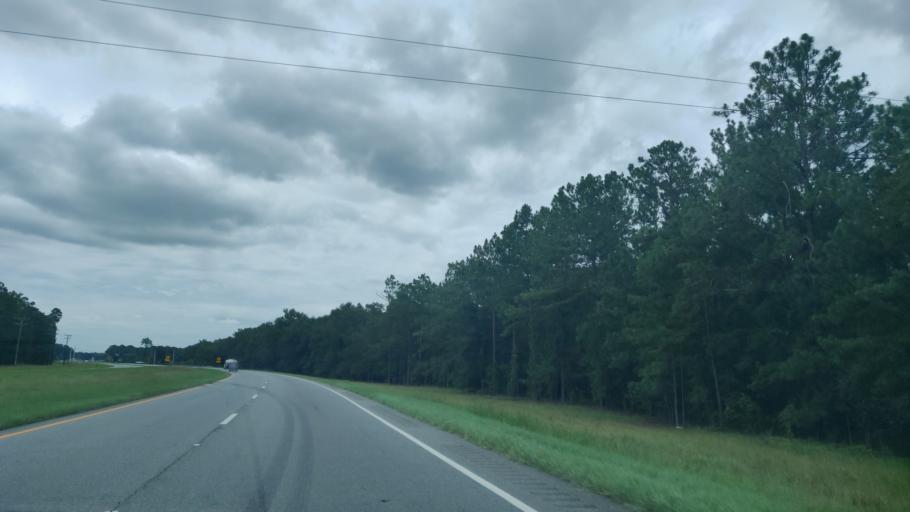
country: US
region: Georgia
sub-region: Dougherty County
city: Putney
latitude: 31.5562
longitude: -84.0033
